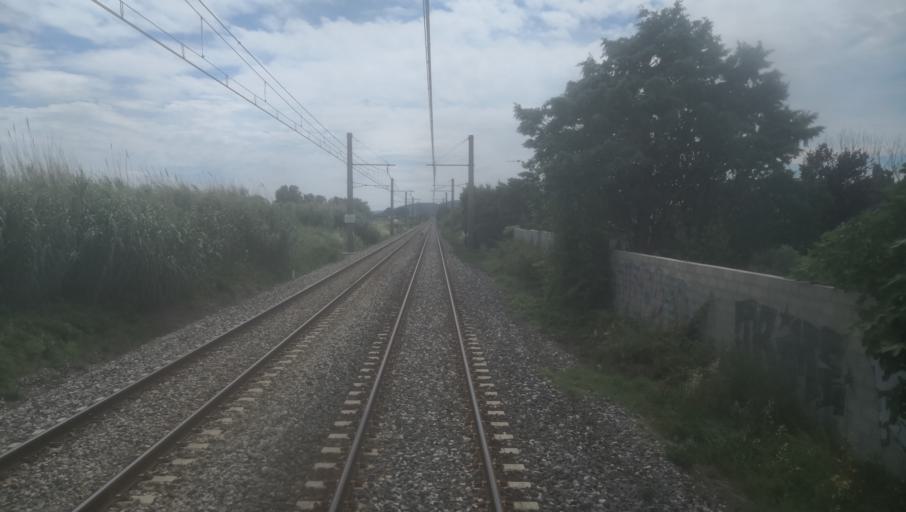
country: FR
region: Languedoc-Roussillon
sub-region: Departement de l'Herault
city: Mireval
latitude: 43.5077
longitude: 3.8088
